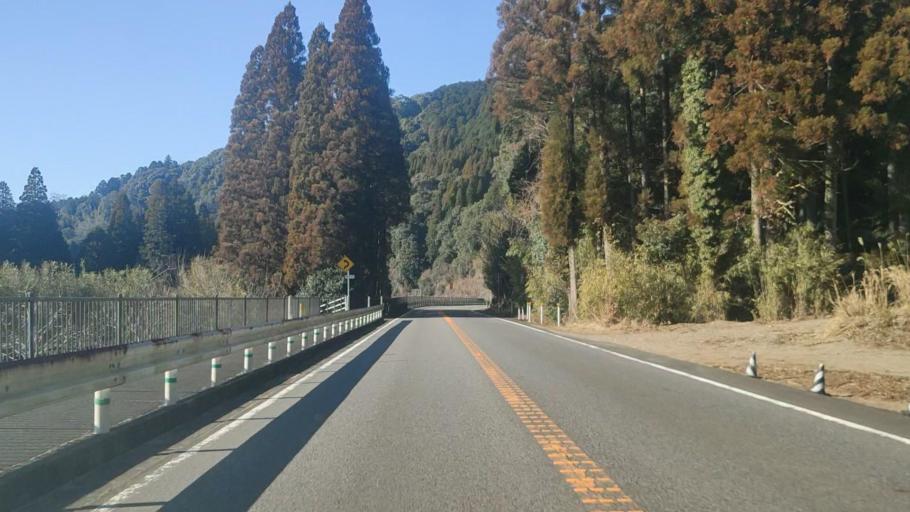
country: JP
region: Oita
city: Usuki
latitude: 33.0073
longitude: 131.7148
